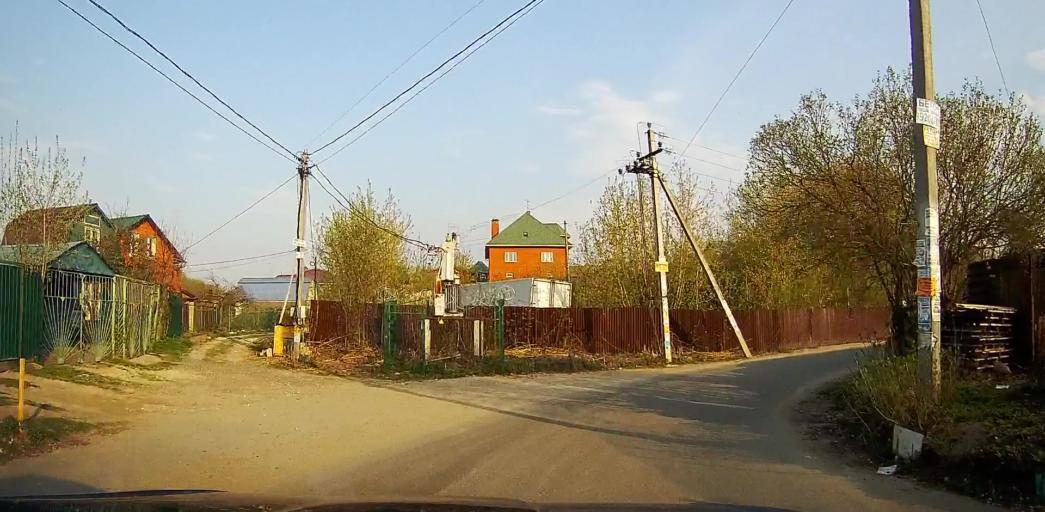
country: RU
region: Moskovskaya
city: Andreyevskoye
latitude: 55.5433
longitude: 37.9754
